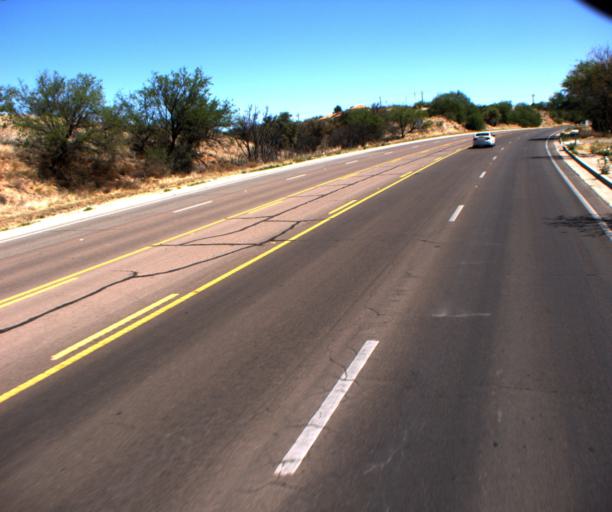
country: US
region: Arizona
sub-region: Santa Cruz County
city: Nogales
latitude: 31.3582
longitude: -110.9152
